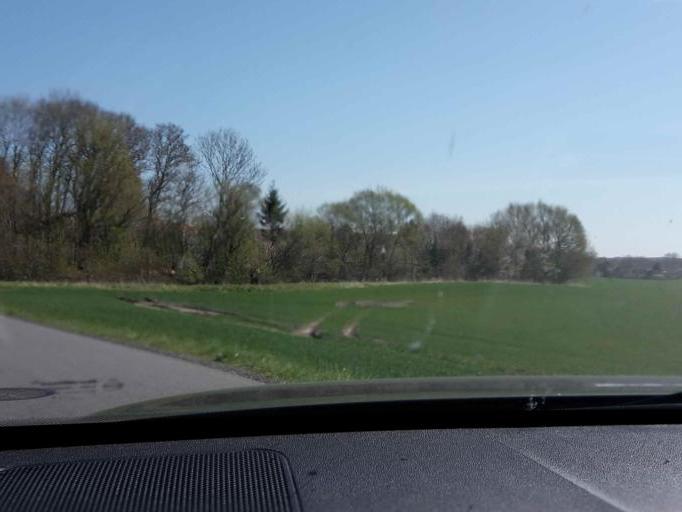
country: DK
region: South Denmark
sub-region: Odense Kommune
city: Bellinge
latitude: 55.3699
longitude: 10.3177
